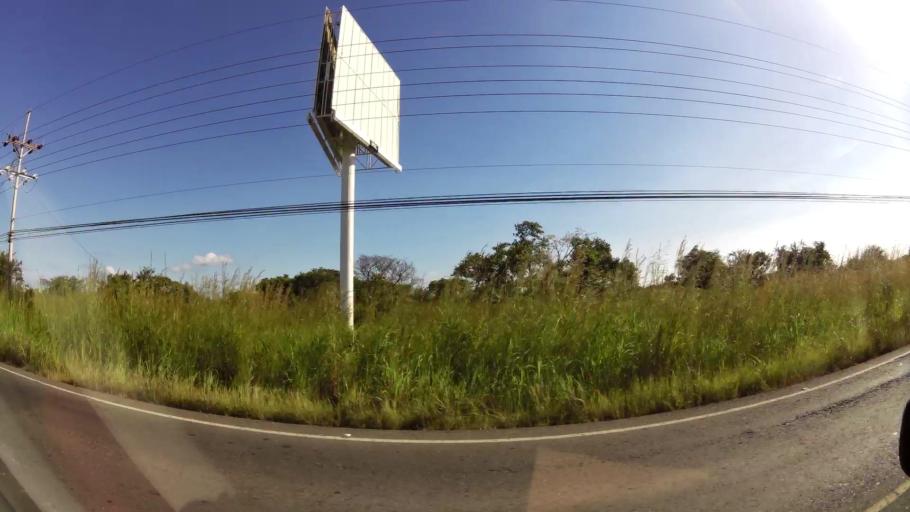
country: CR
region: Guanacaste
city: Liberia
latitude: 10.5914
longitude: -85.5418
